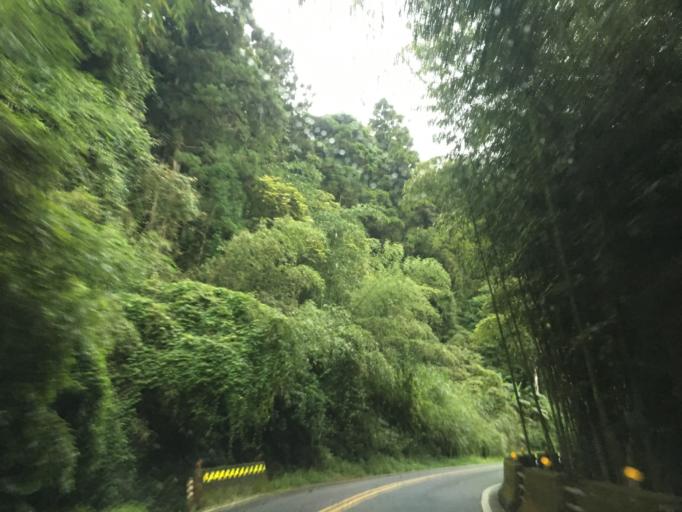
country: TW
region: Taiwan
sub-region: Chiayi
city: Jiayi Shi
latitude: 23.4869
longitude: 120.6995
